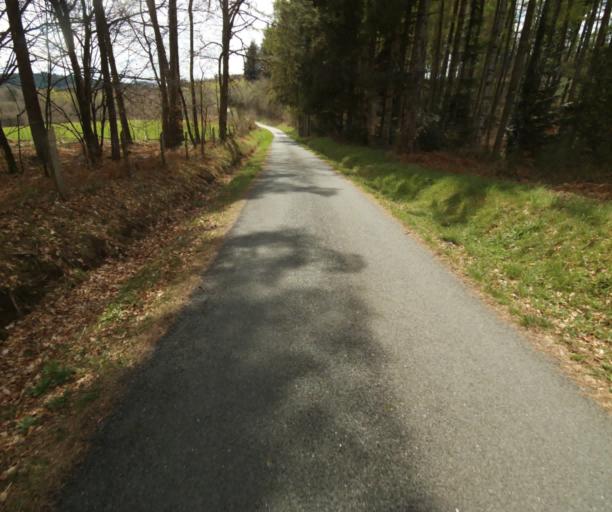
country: FR
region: Limousin
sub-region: Departement de la Correze
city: Correze
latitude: 45.3758
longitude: 1.9636
